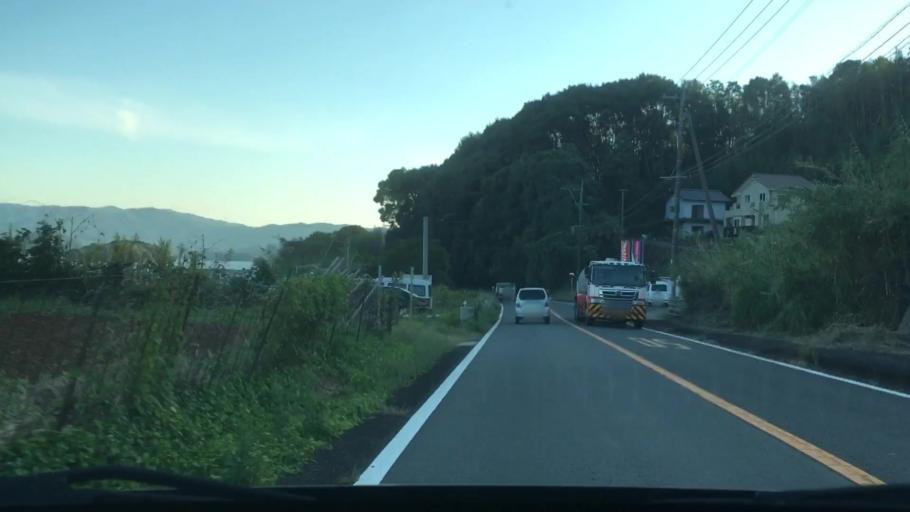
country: JP
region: Nagasaki
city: Sasebo
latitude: 33.0320
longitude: 129.7439
